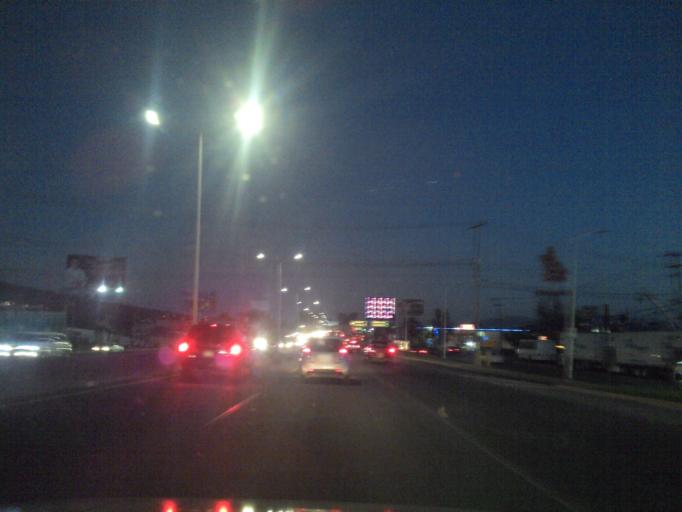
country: MX
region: Jalisco
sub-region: San Pedro Tlaquepaque
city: Paseo del Prado
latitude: 20.6047
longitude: -103.3994
